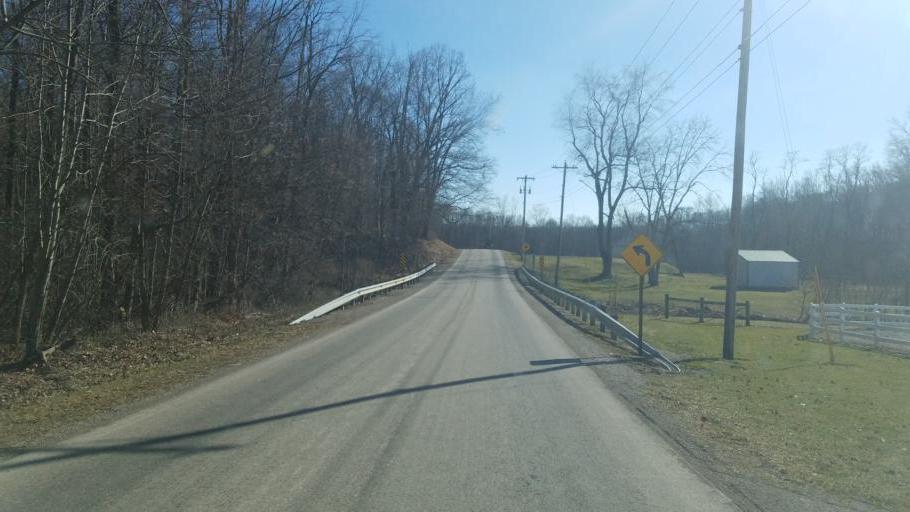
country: US
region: Ohio
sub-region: Knox County
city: Fredericktown
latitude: 40.5594
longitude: -82.6048
